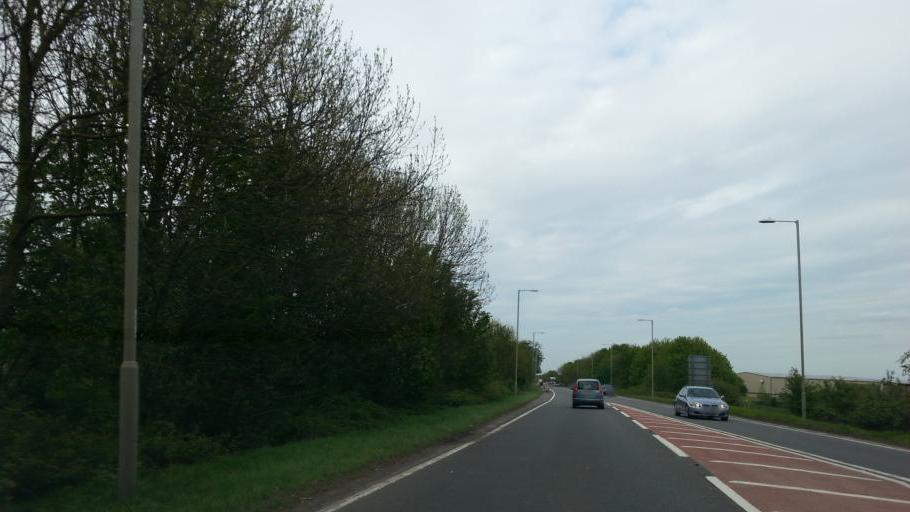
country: GB
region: England
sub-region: Cambridgeshire
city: Doddington
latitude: 52.5046
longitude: 0.0833
